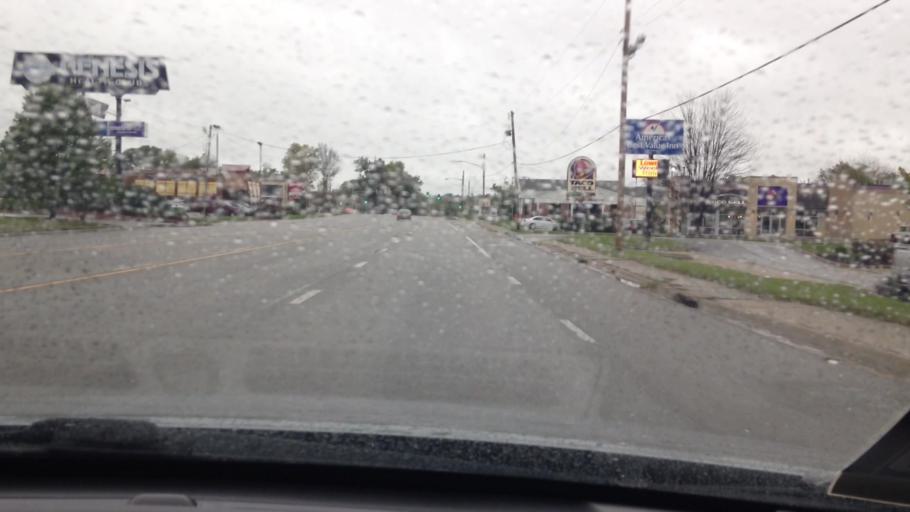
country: US
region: Kansas
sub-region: Leavenworth County
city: Leavenworth
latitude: 39.2869
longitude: -94.9053
